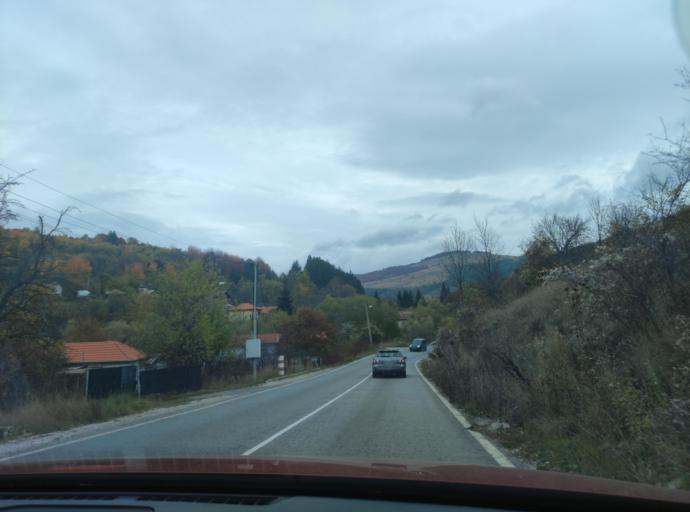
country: BG
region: Sofiya
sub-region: Obshtina Godech
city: Godech
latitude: 43.0691
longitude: 23.1078
